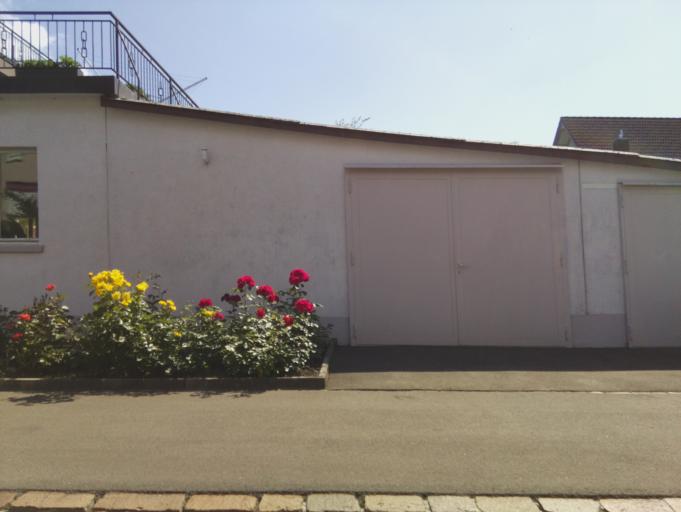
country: CH
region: Glarus
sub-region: Glarus
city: Niederurnen
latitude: 47.1229
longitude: 9.0556
